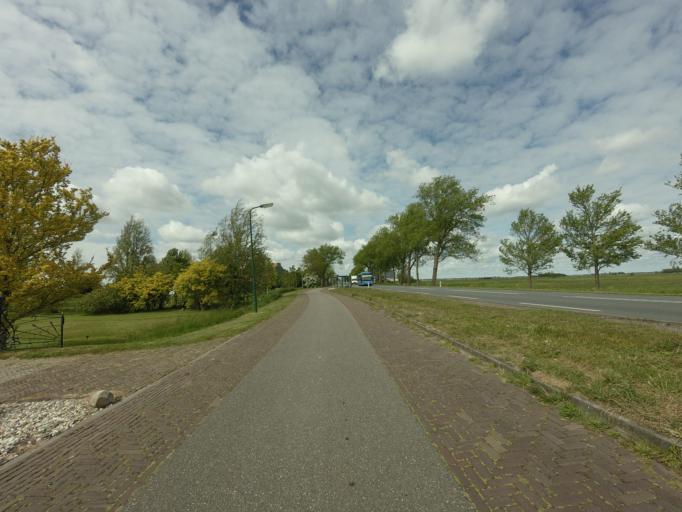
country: NL
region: Friesland
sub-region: Sudwest Fryslan
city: Woudsend
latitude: 52.9738
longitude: 5.6497
